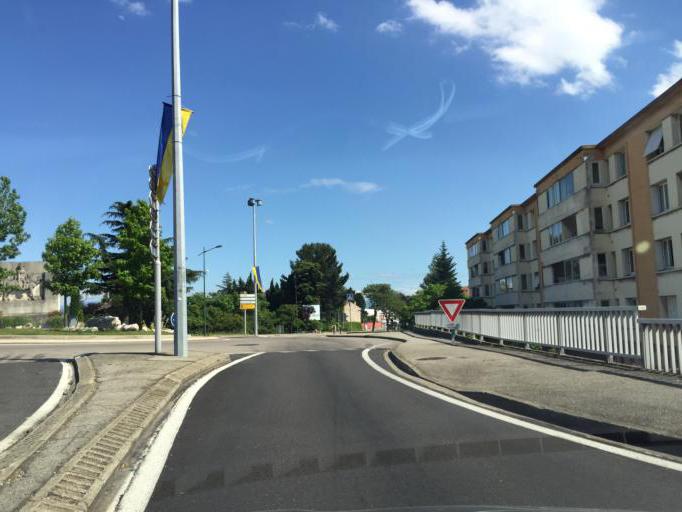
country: FR
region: Rhone-Alpes
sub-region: Departement de l'Ardeche
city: Tournon-sur-Rhone
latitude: 45.0655
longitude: 4.8396
